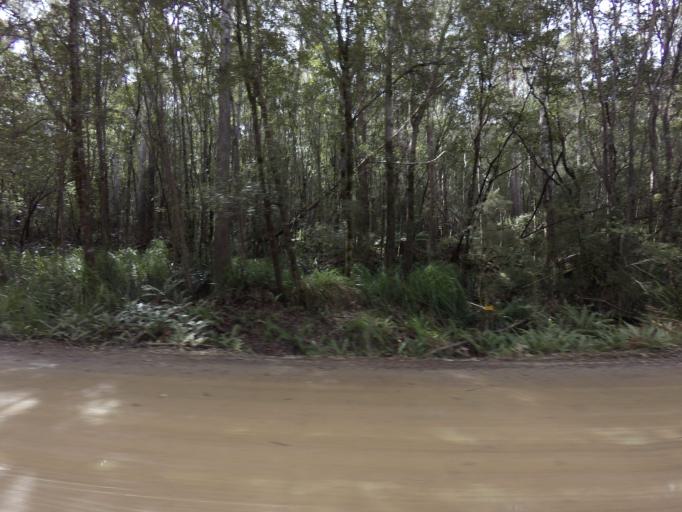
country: AU
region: Tasmania
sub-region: Huon Valley
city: Geeveston
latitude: -43.4117
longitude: 146.8733
